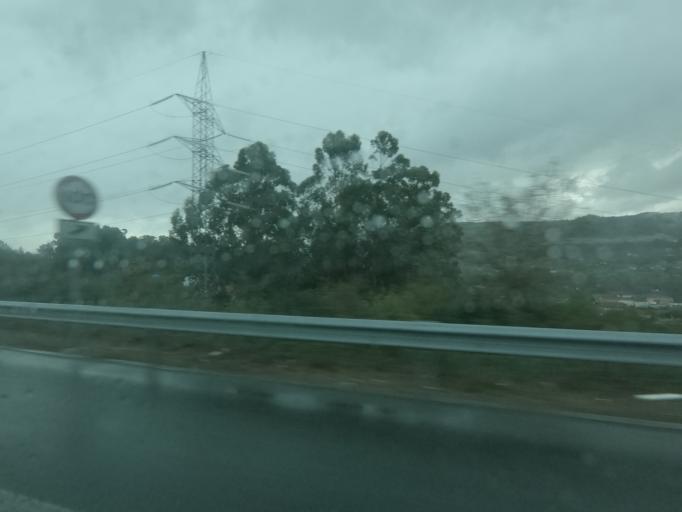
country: ES
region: Galicia
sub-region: Provincia de Pontevedra
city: Pontevedra
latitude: 42.3888
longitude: -8.6405
